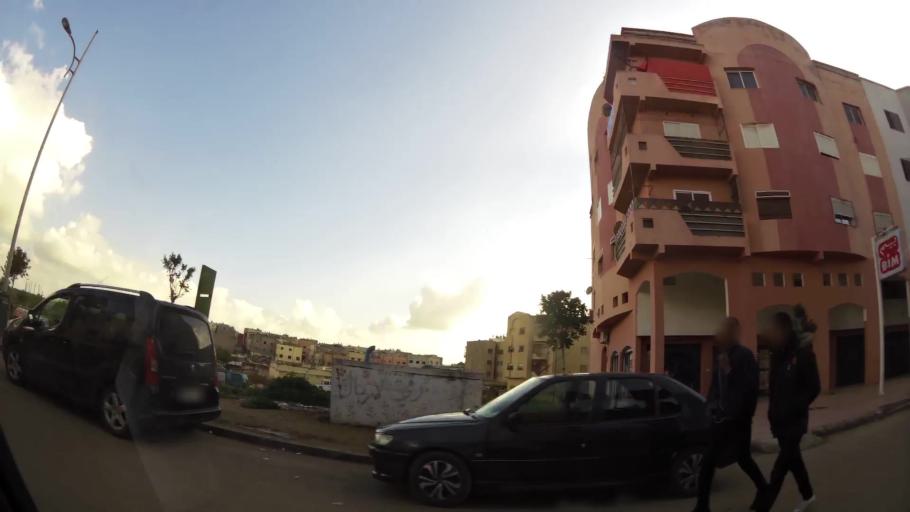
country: MA
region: Chaouia-Ouardigha
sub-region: Settat Province
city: Settat
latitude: 33.0037
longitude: -7.6324
